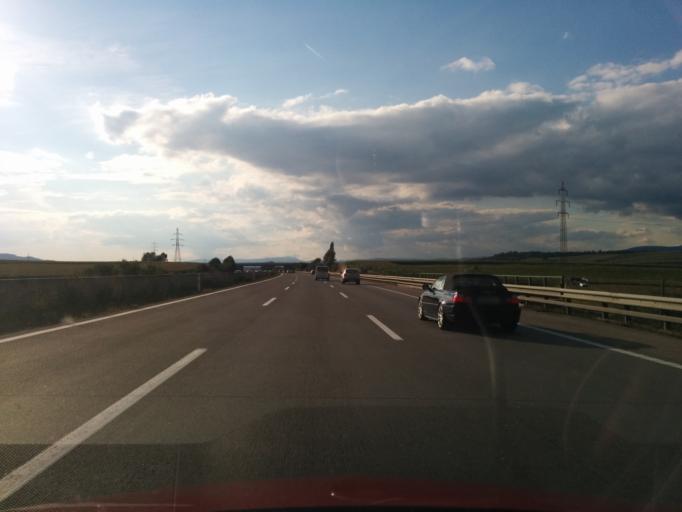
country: AT
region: Lower Austria
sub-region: Politischer Bezirk Sankt Polten
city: Haunoldstein
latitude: 48.1796
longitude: 15.4553
